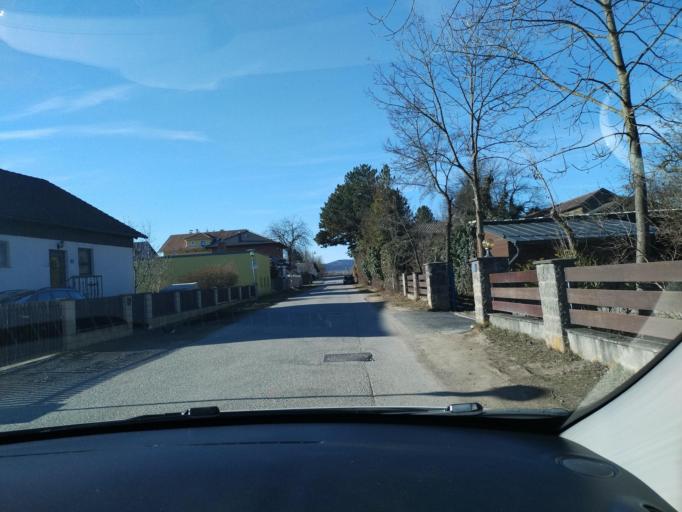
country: AT
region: Lower Austria
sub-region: Politischer Bezirk Wiener Neustadt
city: Lanzenkirchen
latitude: 47.7489
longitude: 16.2532
